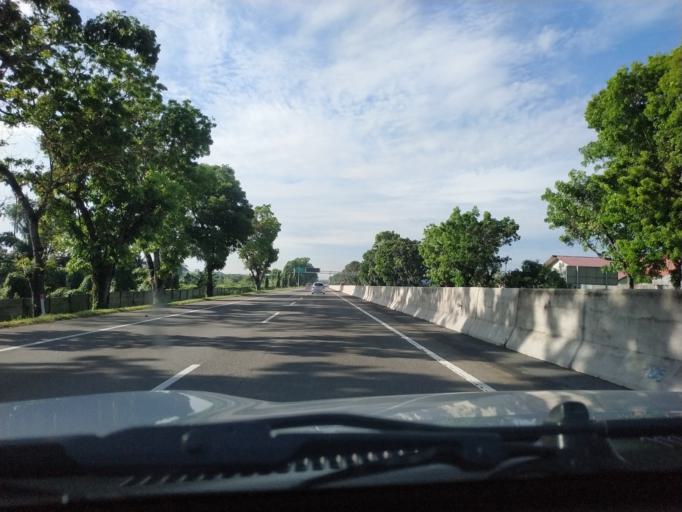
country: ID
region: North Sumatra
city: Medan
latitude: 3.5598
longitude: 98.7256
